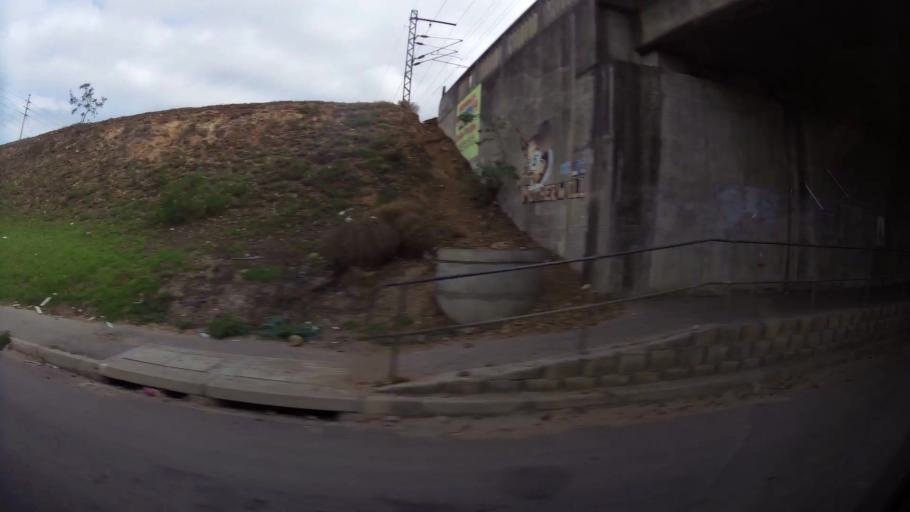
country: ZA
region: Eastern Cape
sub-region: Nelson Mandela Bay Metropolitan Municipality
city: Port Elizabeth
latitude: -33.8154
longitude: 25.6317
